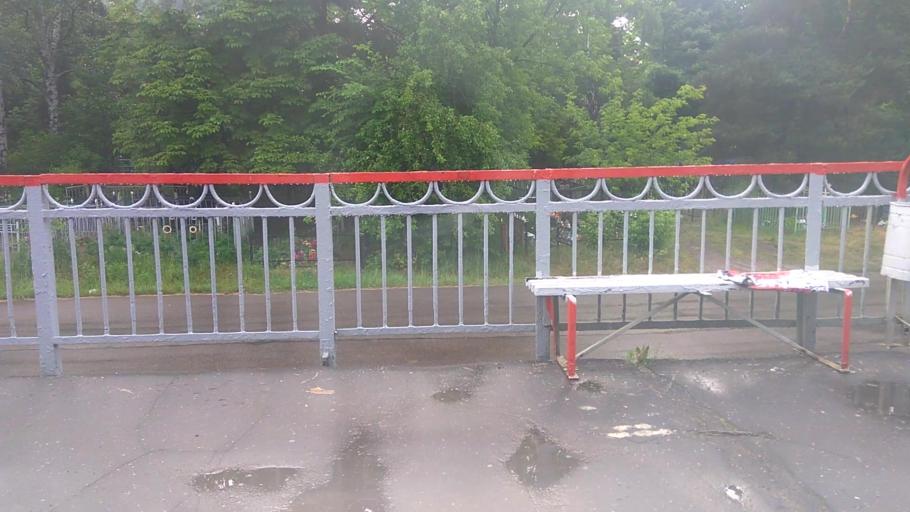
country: RU
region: Moskovskaya
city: Kashira
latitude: 54.8698
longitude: 38.1434
